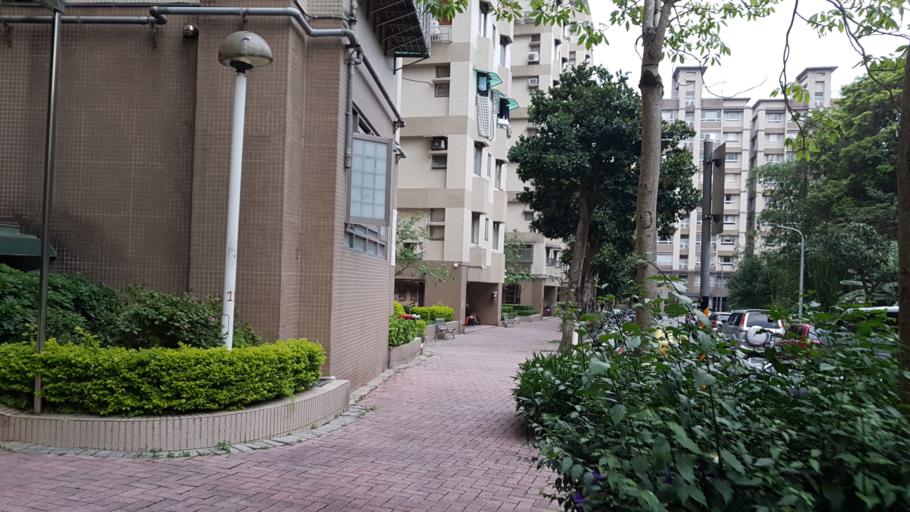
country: TW
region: Taipei
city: Taipei
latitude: 25.0052
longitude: 121.5476
